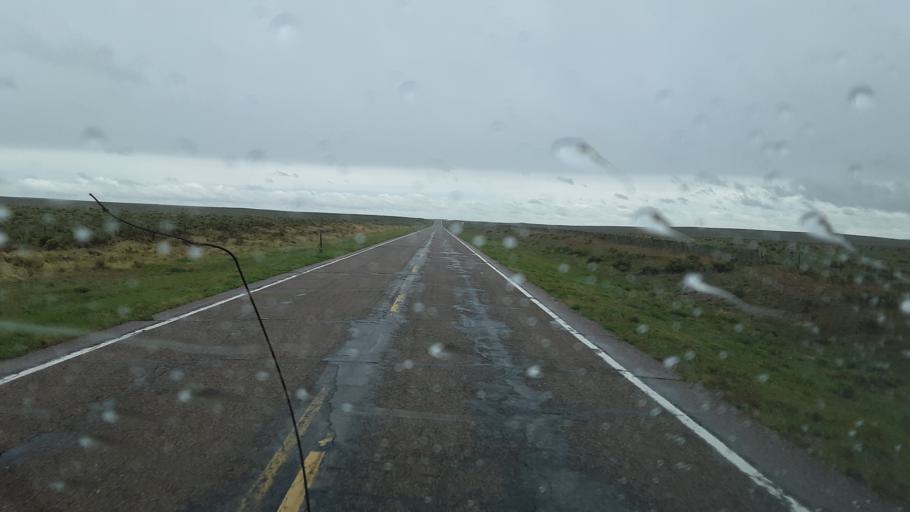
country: US
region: Colorado
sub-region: Lincoln County
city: Hugo
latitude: 38.8497
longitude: -103.2079
